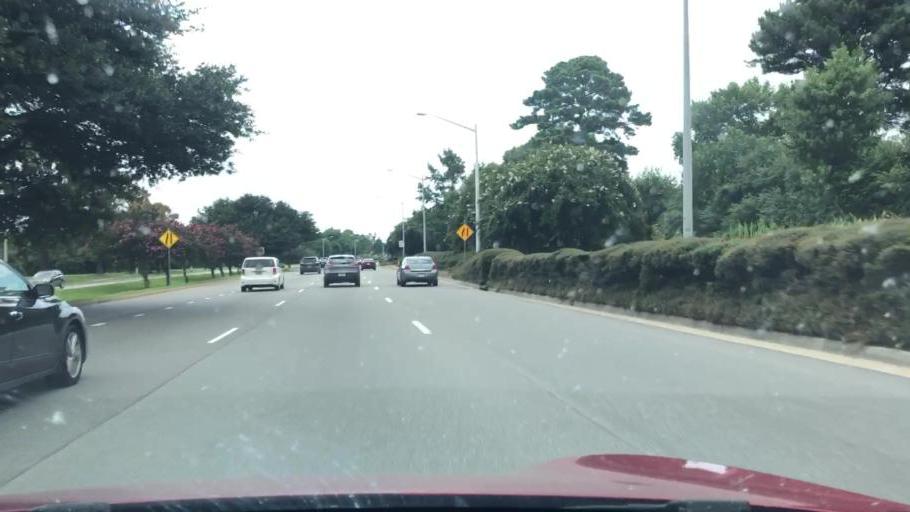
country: US
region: Virginia
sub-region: City of Chesapeake
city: Chesapeake
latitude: 36.8492
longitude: -76.1365
